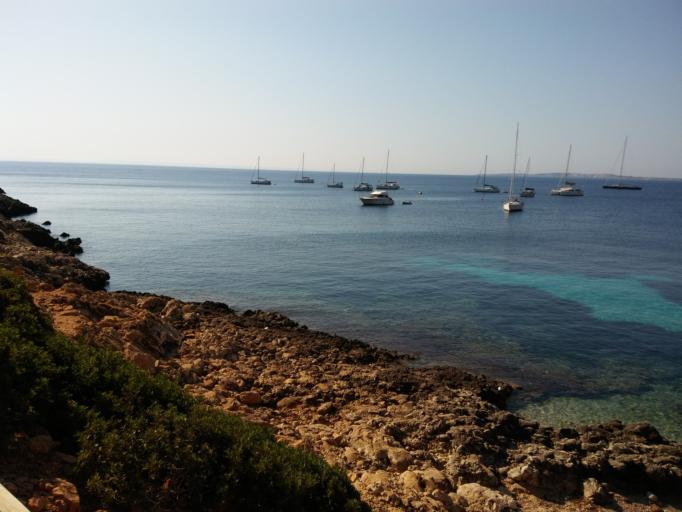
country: IT
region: Sicily
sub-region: Trapani
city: Favignana
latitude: 37.9899
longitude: 12.3452
